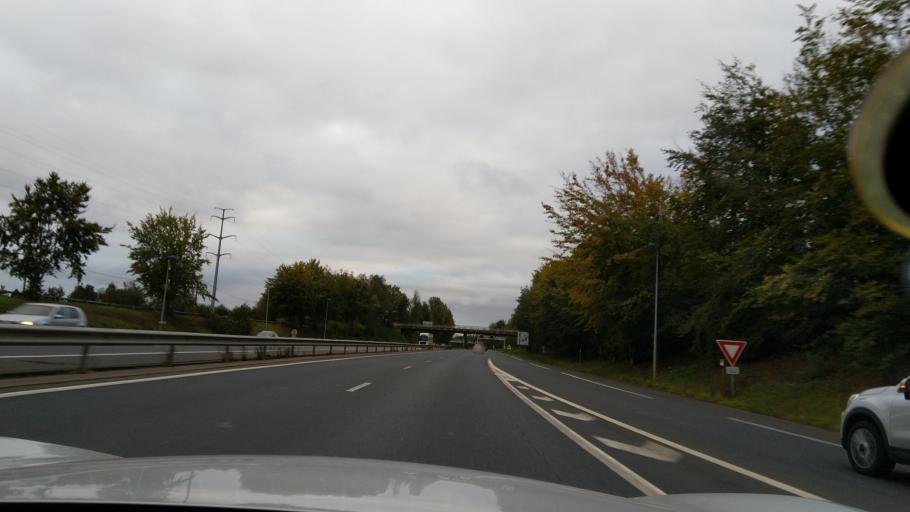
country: FR
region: Haute-Normandie
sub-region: Departement de la Seine-Maritime
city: Bois-Guillaume
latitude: 49.4766
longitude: 1.1369
